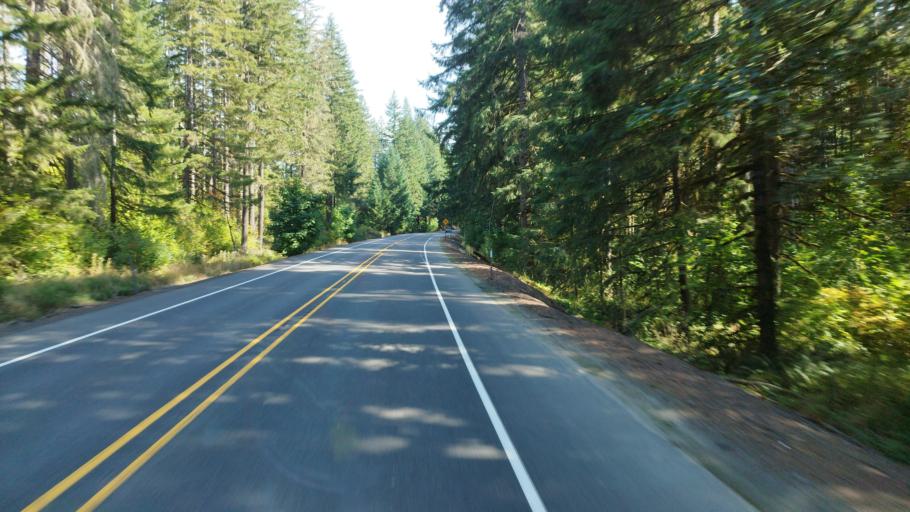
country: US
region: Oregon
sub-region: Columbia County
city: Vernonia
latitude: 45.7796
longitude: -123.3395
